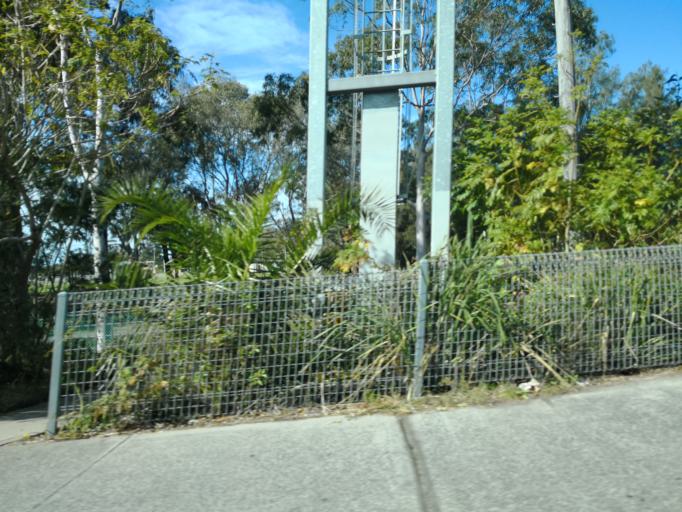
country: AU
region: New South Wales
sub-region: Gosford Shire
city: Point Clare
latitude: -33.4279
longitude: 151.3236
